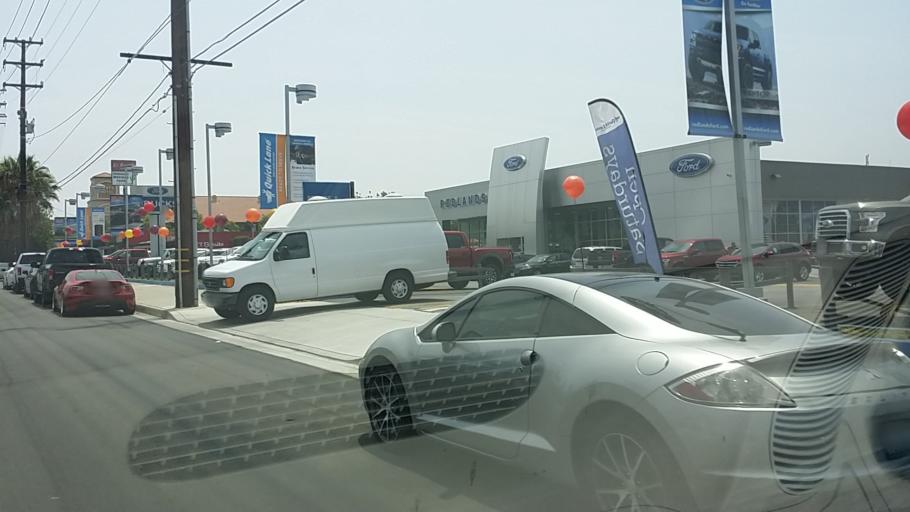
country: US
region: California
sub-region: San Bernardino County
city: Redlands
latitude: 34.0629
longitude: -117.1989
